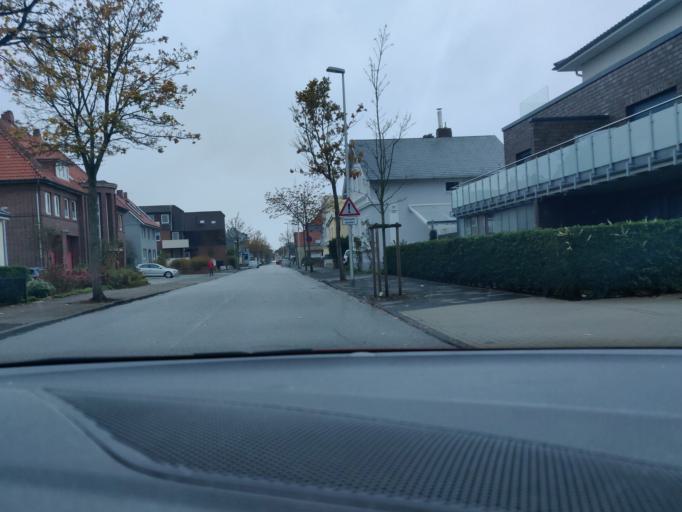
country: DE
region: Lower Saxony
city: Cuxhaven
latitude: 53.8835
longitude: 8.6698
